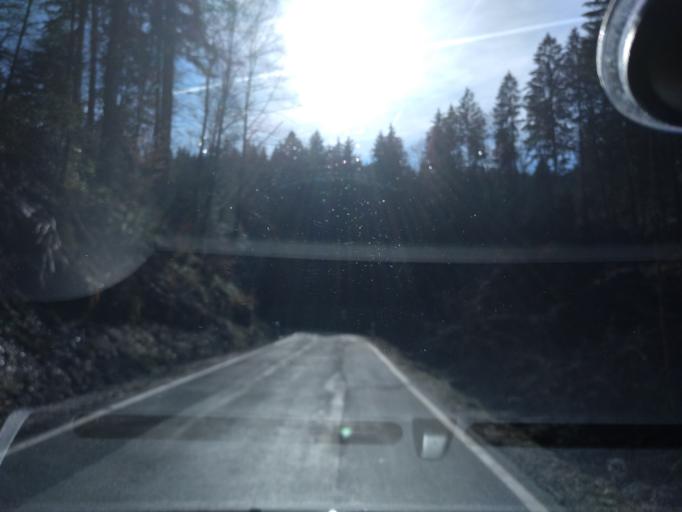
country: DE
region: Baden-Wuerttemberg
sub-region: Regierungsbezirk Stuttgart
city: Mainhardt
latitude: 49.0873
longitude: 9.5500
